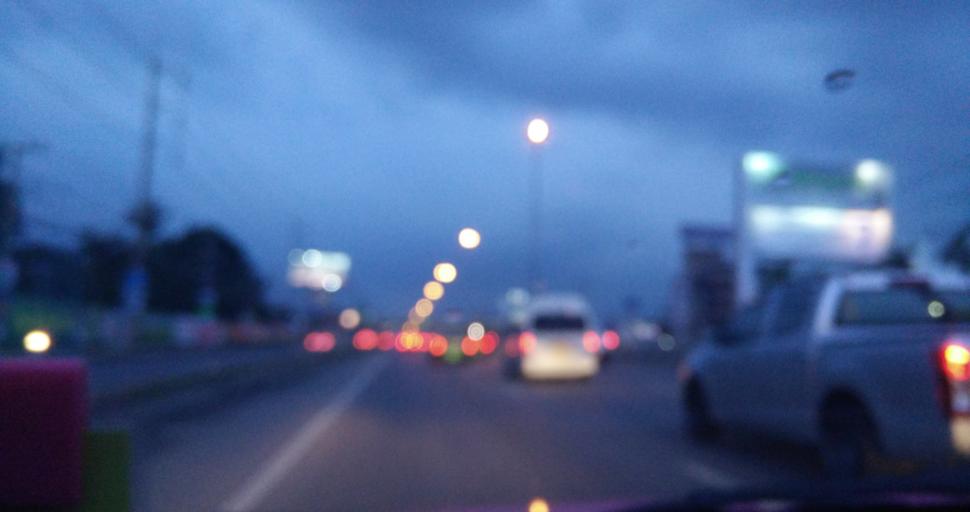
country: TH
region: Pathum Thani
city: Khlong Luang
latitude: 14.0130
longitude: 100.6152
